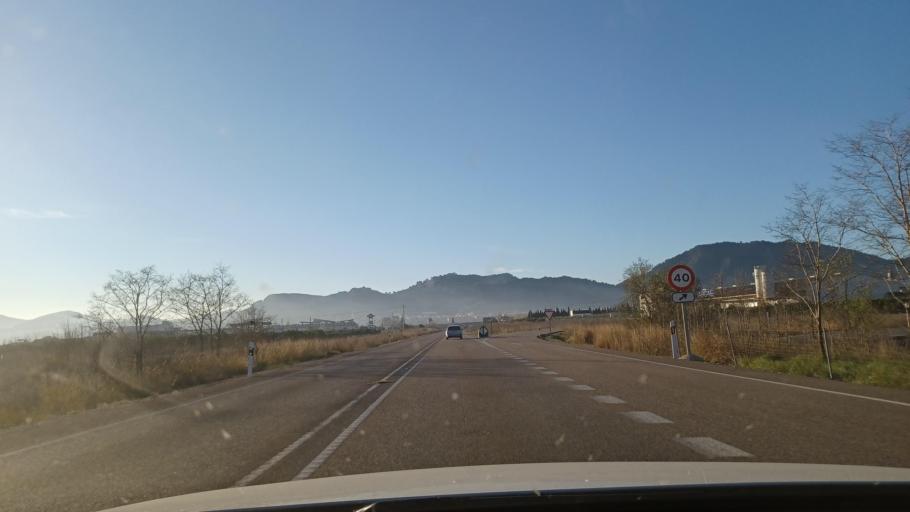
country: ES
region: Valencia
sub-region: Provincia de Valencia
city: Llosa de Ranes
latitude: 39.0088
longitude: -0.5322
